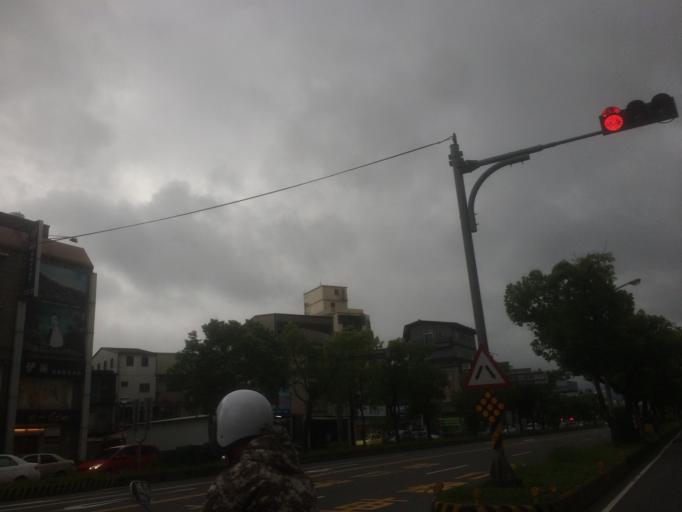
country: TW
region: Taiwan
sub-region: Yilan
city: Yilan
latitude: 24.6742
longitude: 121.7634
